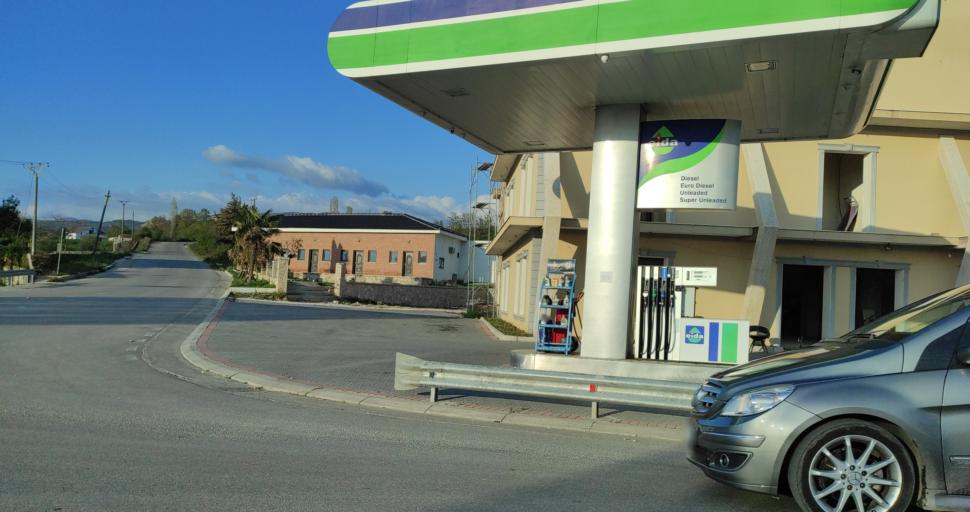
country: AL
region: Durres
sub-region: Rrethi i Krujes
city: Fushe-Kruje
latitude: 41.4912
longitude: 19.7223
